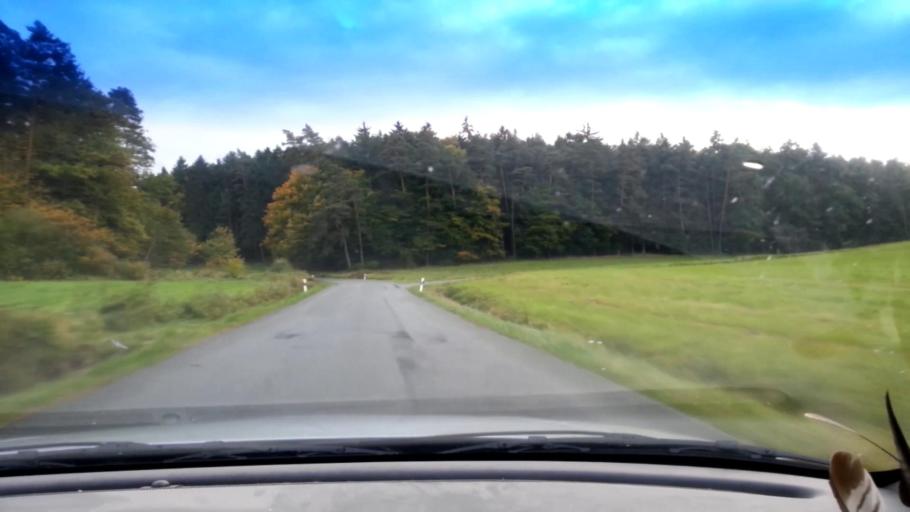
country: DE
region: Bavaria
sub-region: Upper Franconia
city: Burgebrach
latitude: 49.8044
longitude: 10.7061
